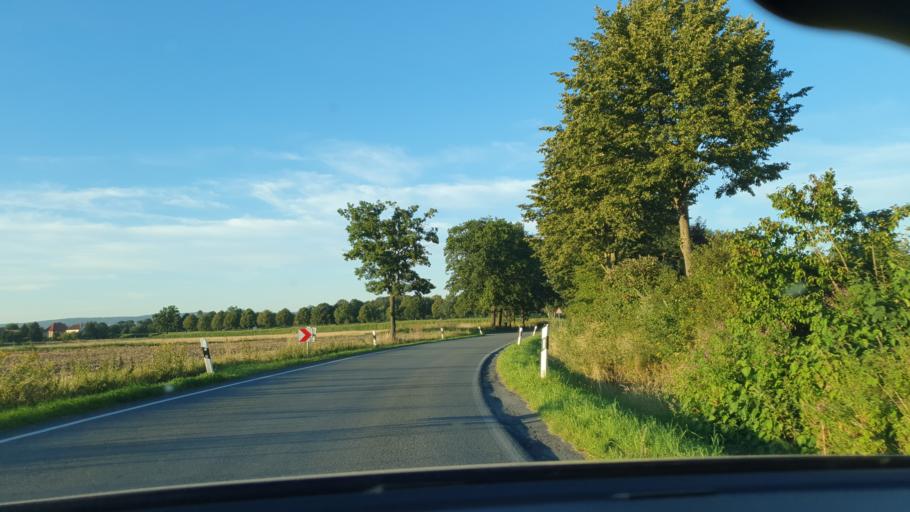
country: DE
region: North Rhine-Westphalia
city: Spenge
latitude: 52.1784
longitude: 8.5097
